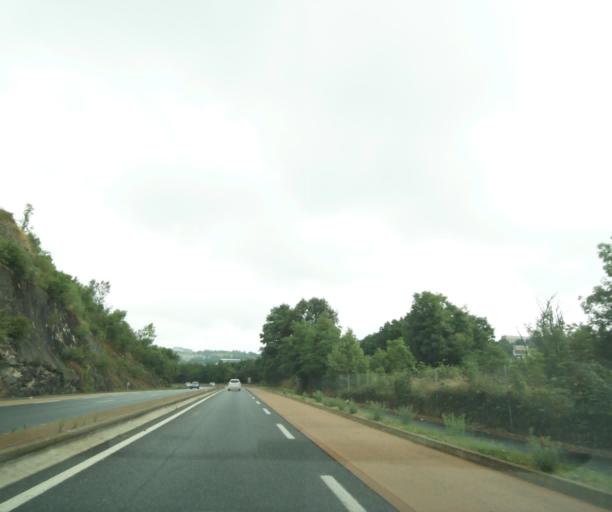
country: FR
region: Midi-Pyrenees
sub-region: Departement de l'Aveyron
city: Olemps
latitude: 44.3448
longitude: 2.5593
